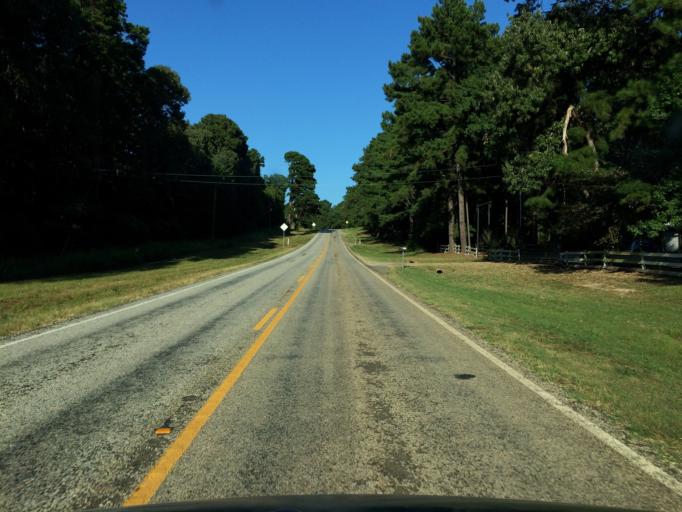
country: US
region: Texas
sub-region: Wood County
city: Hawkins
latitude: 32.6400
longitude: -95.2546
